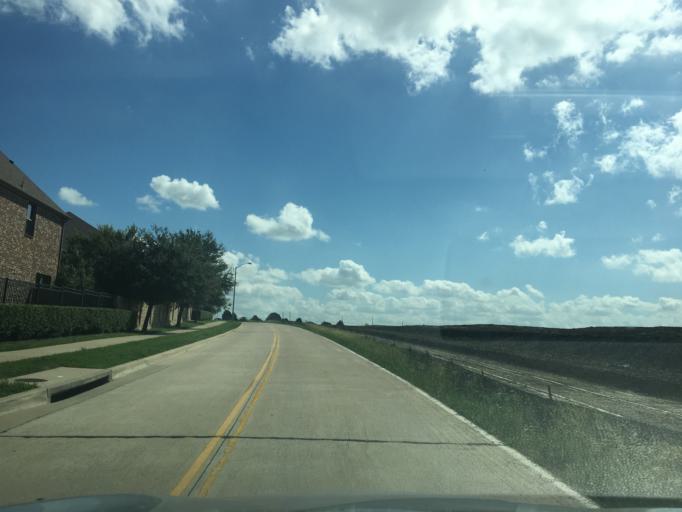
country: US
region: Texas
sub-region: Dallas County
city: Sachse
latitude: 32.9579
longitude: -96.5747
